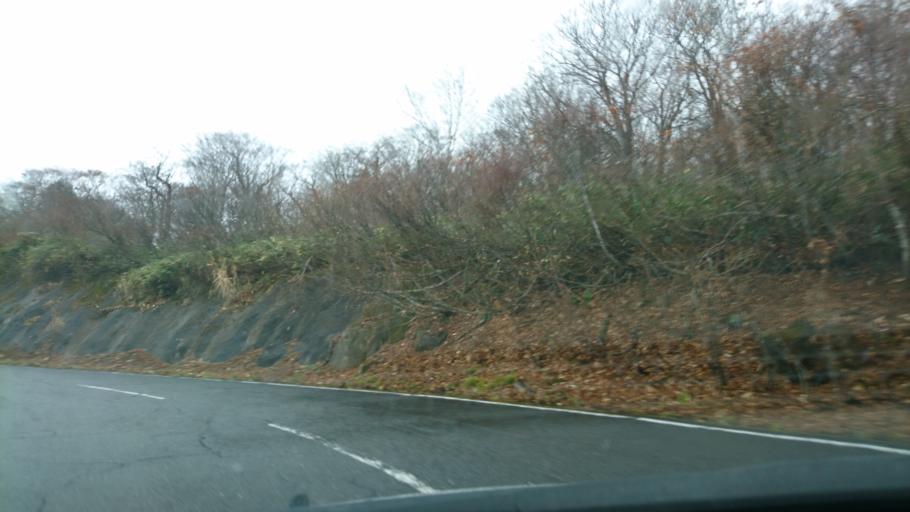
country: JP
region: Iwate
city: Ichinoseki
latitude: 38.9452
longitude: 140.8129
